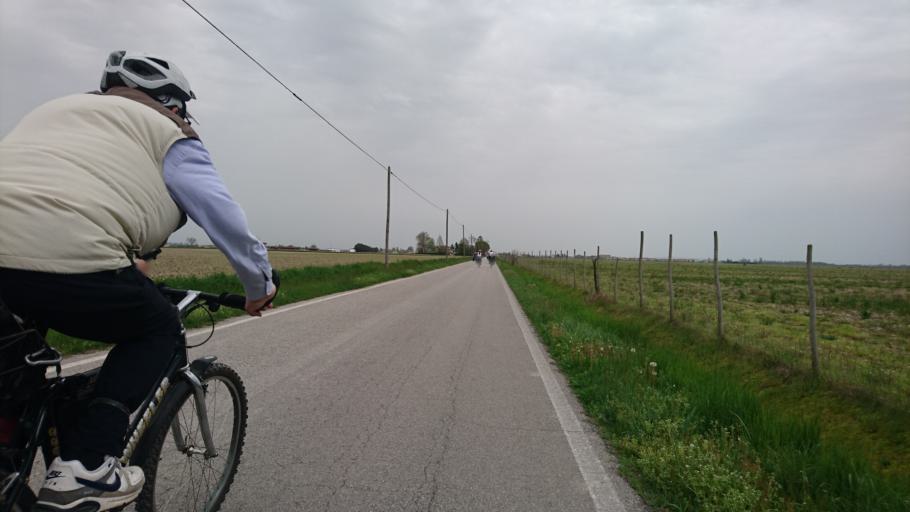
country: IT
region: Veneto
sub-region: Provincia di Venezia
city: Lugugnana
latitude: 45.6989
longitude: 12.9259
